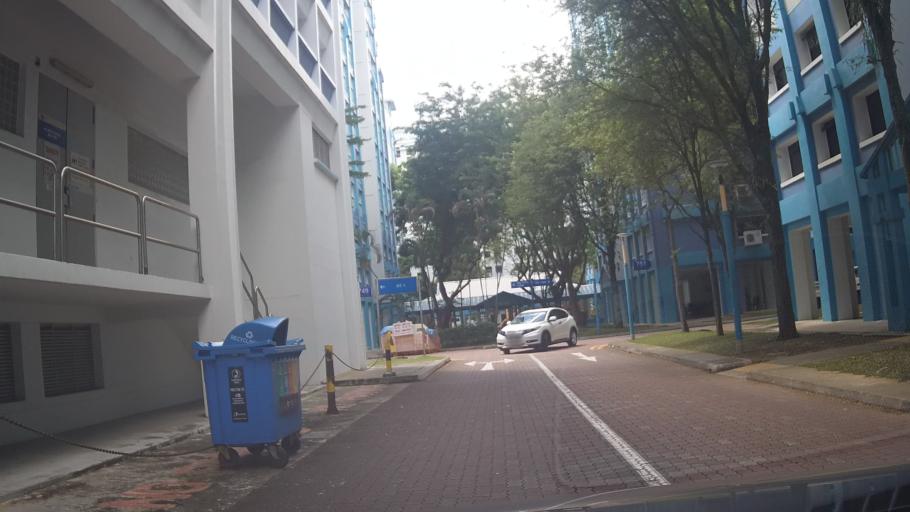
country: MY
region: Johor
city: Johor Bahru
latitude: 1.4455
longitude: 103.7951
